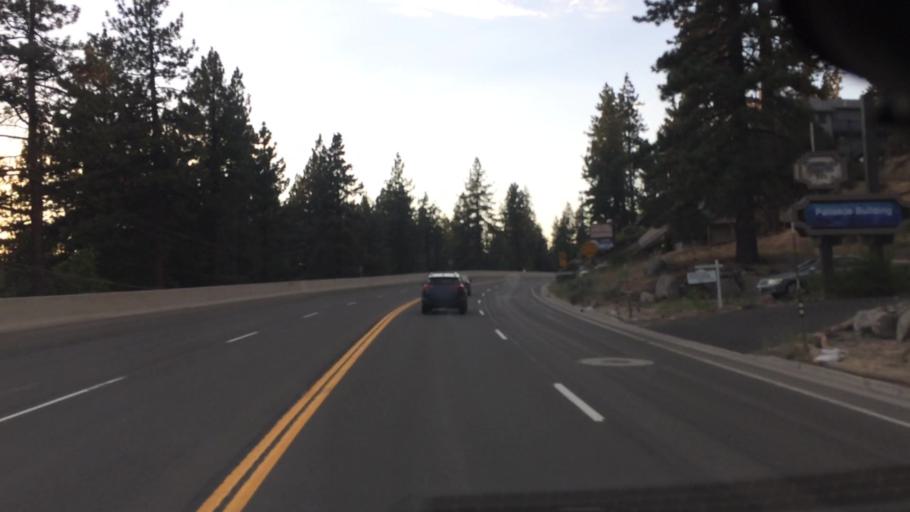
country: US
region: Nevada
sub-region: Douglas County
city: Kingsbury
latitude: 38.9987
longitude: -119.9549
